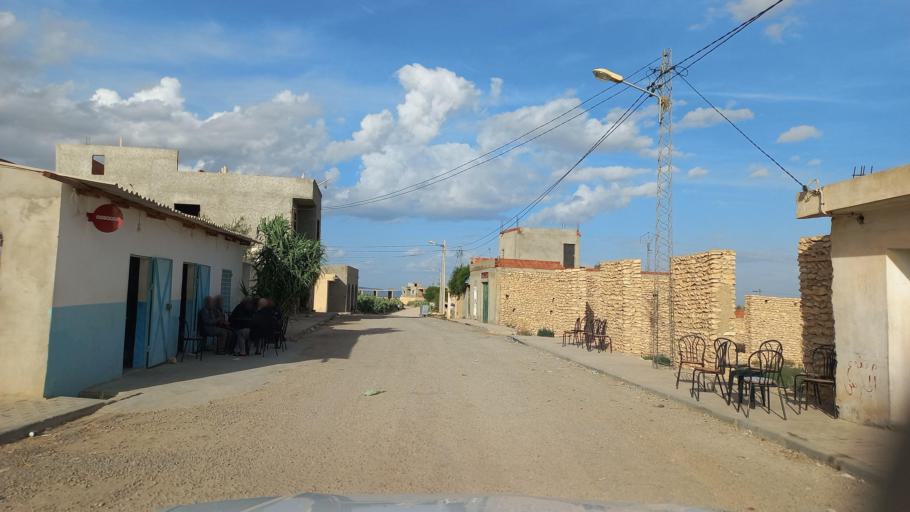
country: TN
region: Al Qasrayn
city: Sbiba
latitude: 35.4456
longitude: 9.0795
